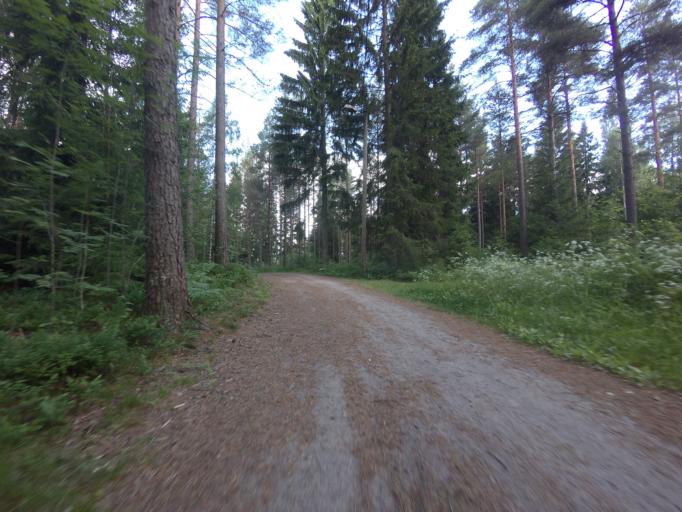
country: FI
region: Uusimaa
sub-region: Helsinki
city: Espoo
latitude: 60.1828
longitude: 24.6330
